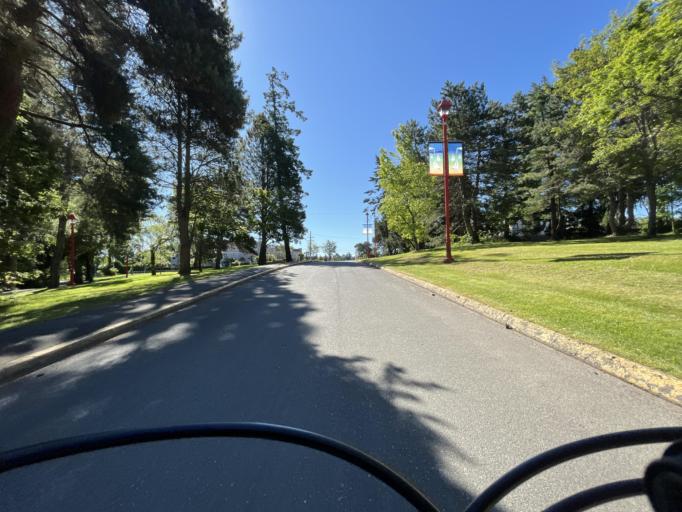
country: CA
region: British Columbia
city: Victoria
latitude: 48.4459
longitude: -123.4018
